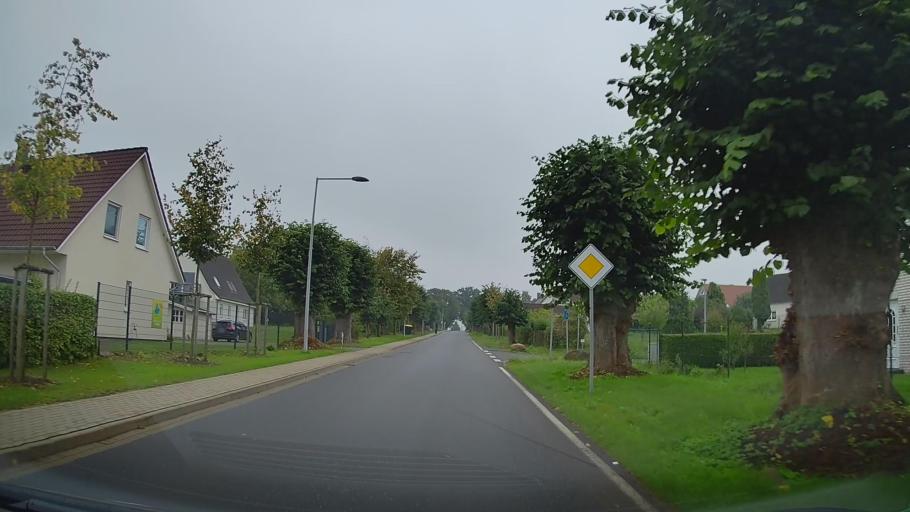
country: DE
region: Mecklenburg-Vorpommern
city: Gramkow
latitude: 53.9253
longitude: 11.3746
